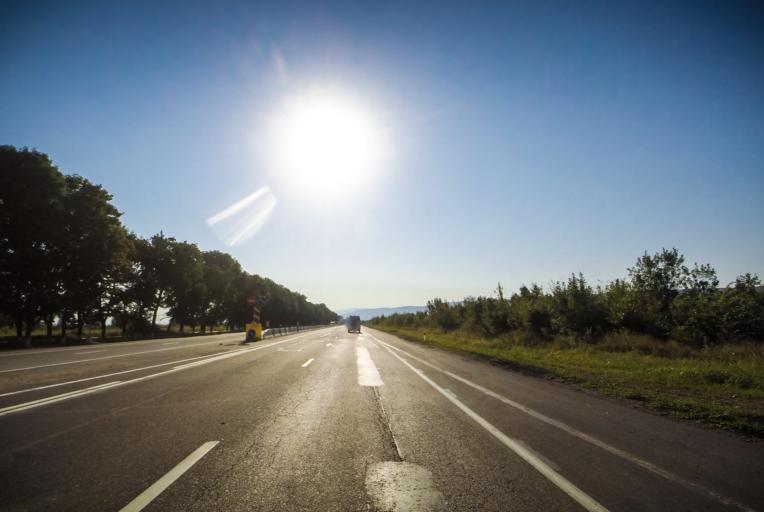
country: RU
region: North Ossetia
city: Zmeyskaya
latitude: 43.3225
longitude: 44.1031
